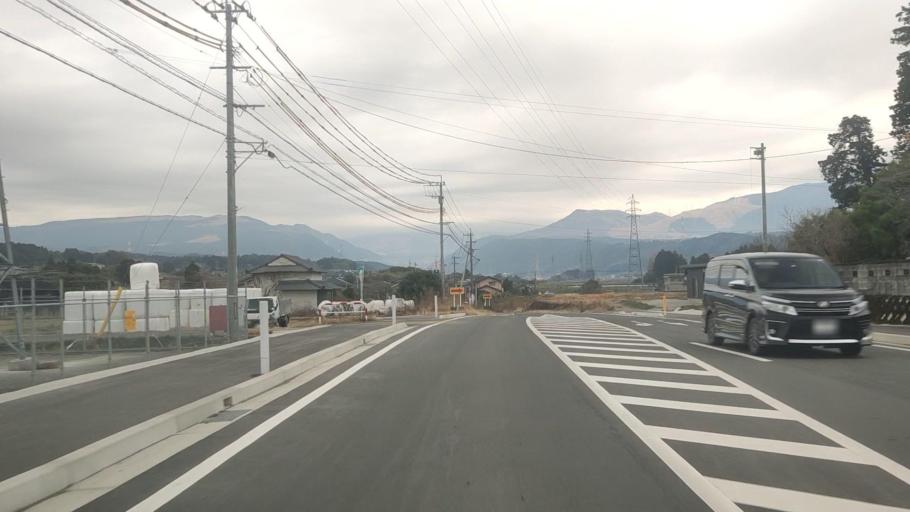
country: JP
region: Kumamoto
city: Ozu
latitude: 32.8651
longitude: 130.8914
